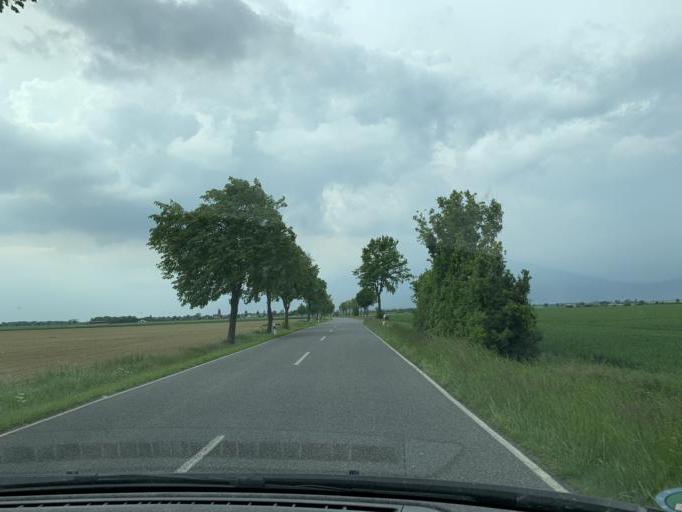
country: DE
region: North Rhine-Westphalia
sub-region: Regierungsbezirk Koln
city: Vettweiss
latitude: 50.7508
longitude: 6.5759
